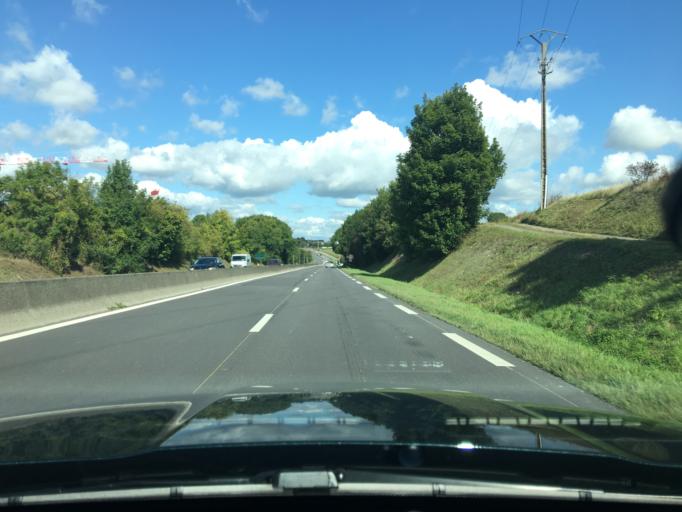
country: FR
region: Ile-de-France
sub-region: Departement du Val-d'Oise
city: Louvres
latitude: 49.0352
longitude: 2.5058
